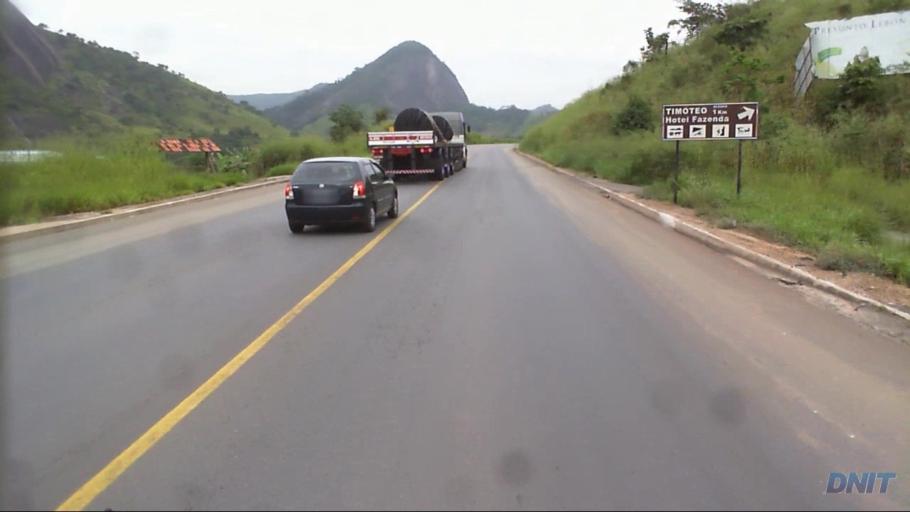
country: BR
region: Minas Gerais
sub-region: Coronel Fabriciano
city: Coronel Fabriciano
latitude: -19.5376
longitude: -42.6755
